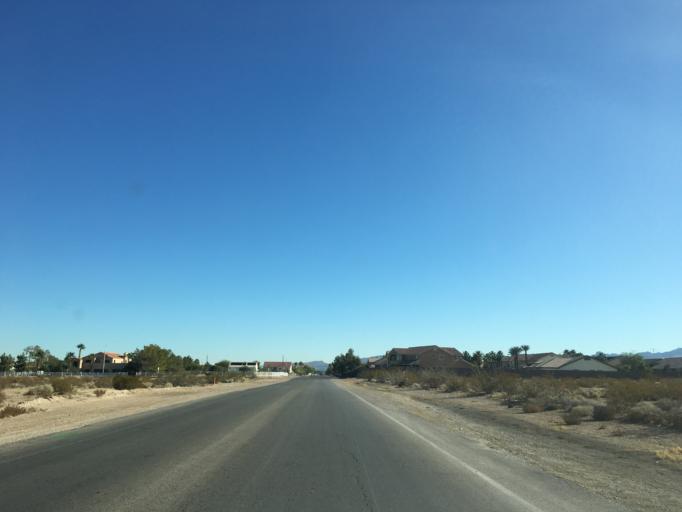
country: US
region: Nevada
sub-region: Clark County
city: Enterprise
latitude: 36.0065
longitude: -115.1678
